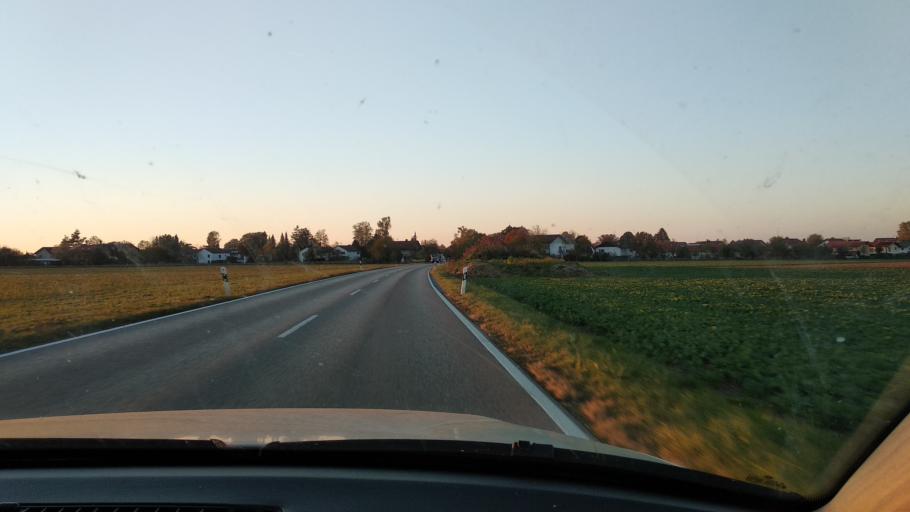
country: DE
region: Bavaria
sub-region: Upper Bavaria
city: Hohenbrunn
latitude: 48.0423
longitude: 11.7076
